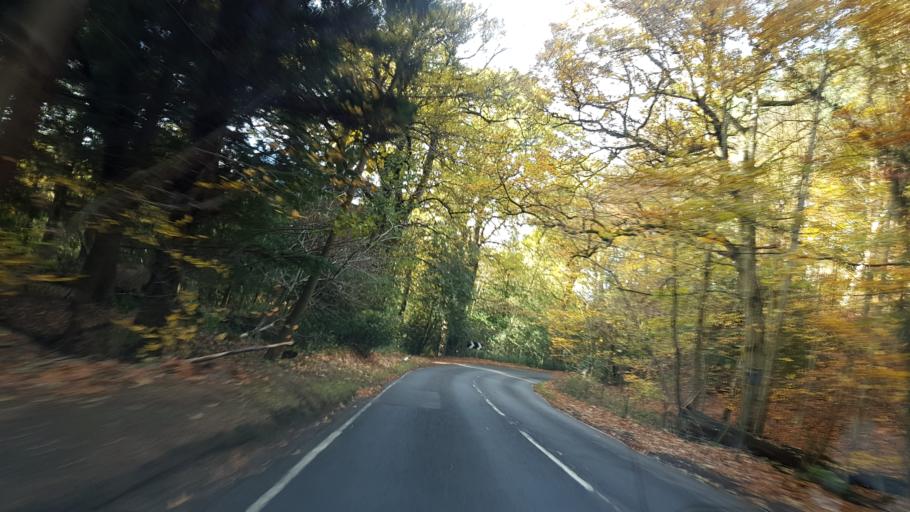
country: GB
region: England
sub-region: Surrey
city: Seale
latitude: 51.2013
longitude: -0.7512
